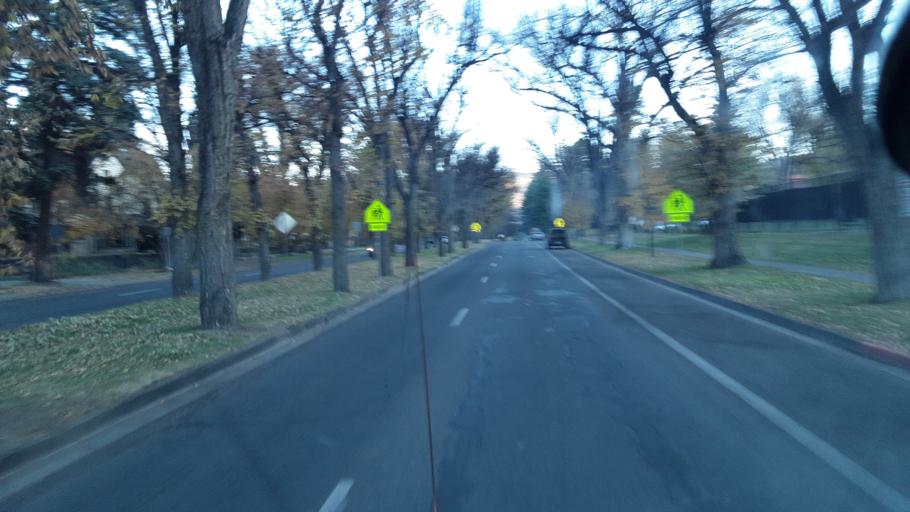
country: US
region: Colorado
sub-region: La Plata County
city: Durango
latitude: 37.2760
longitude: -107.8768
